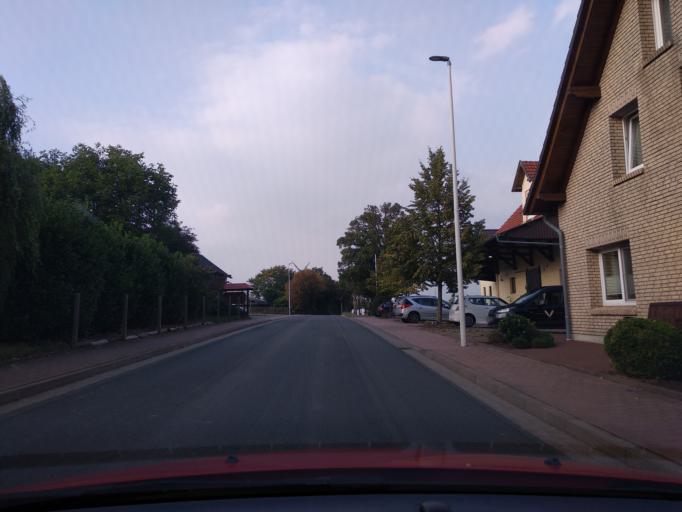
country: DE
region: North Rhine-Westphalia
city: Beverungen
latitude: 51.6240
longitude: 9.3419
